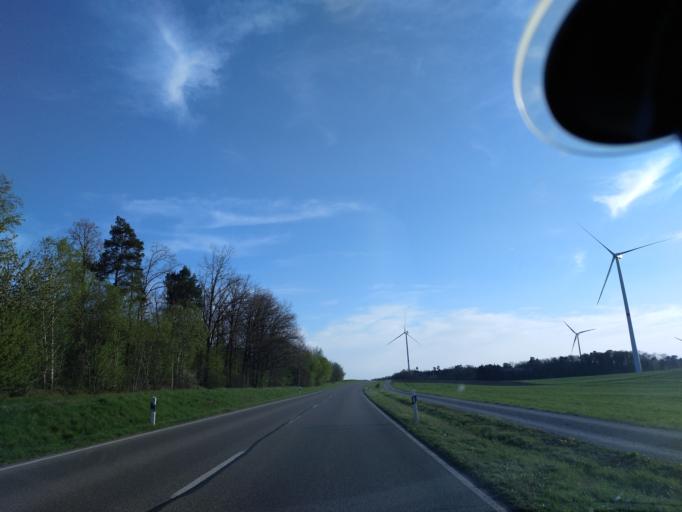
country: DE
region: Baden-Wuerttemberg
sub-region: Regierungsbezirk Stuttgart
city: Kirchberg an der Jagst
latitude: 49.1915
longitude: 9.9722
